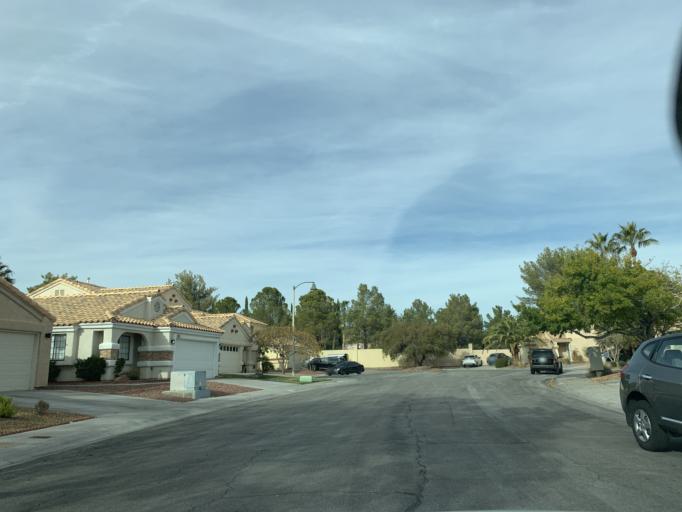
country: US
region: Nevada
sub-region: Clark County
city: Summerlin South
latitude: 36.1365
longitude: -115.3053
